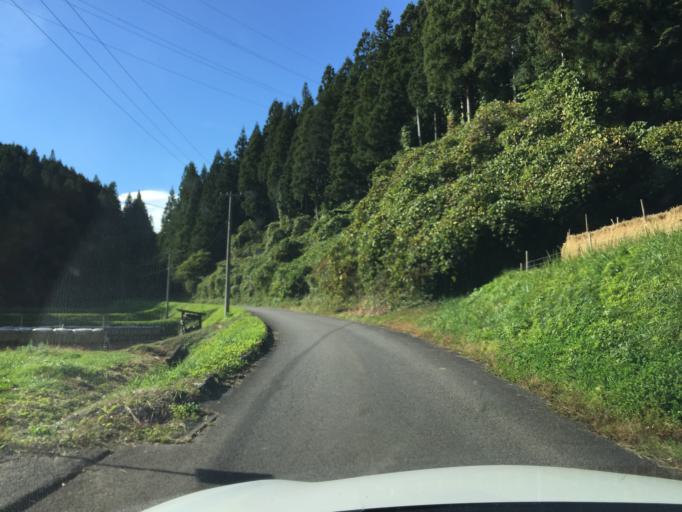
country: JP
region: Fukushima
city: Ishikawa
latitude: 37.1320
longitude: 140.5506
